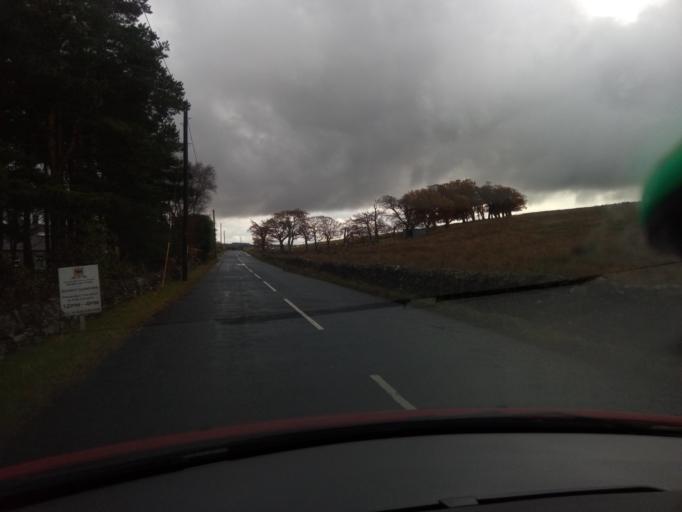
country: GB
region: England
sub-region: Northumberland
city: Birtley
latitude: 55.1263
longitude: -2.2342
